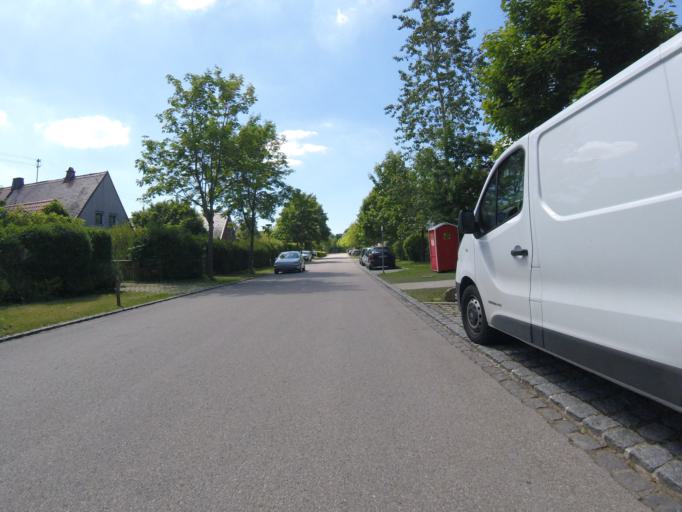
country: DE
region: Bavaria
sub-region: Upper Bavaria
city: Unterhaching
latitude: 48.0853
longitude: 11.6275
